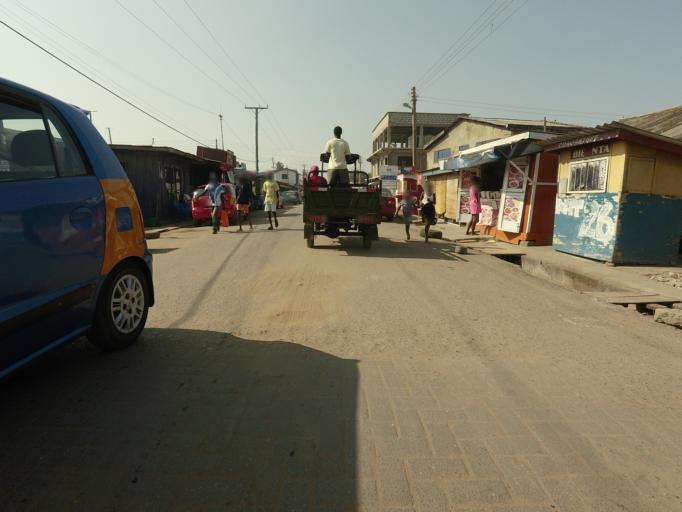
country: GH
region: Greater Accra
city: Teshi Old Town
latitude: 5.5817
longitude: -0.1008
